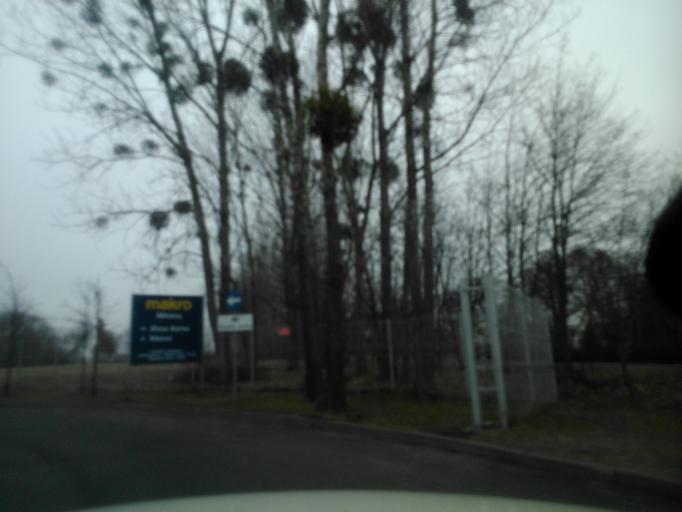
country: PL
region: Kujawsko-Pomorskie
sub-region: Powiat torunski
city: Lubicz Dolny
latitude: 53.0375
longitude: 18.6871
